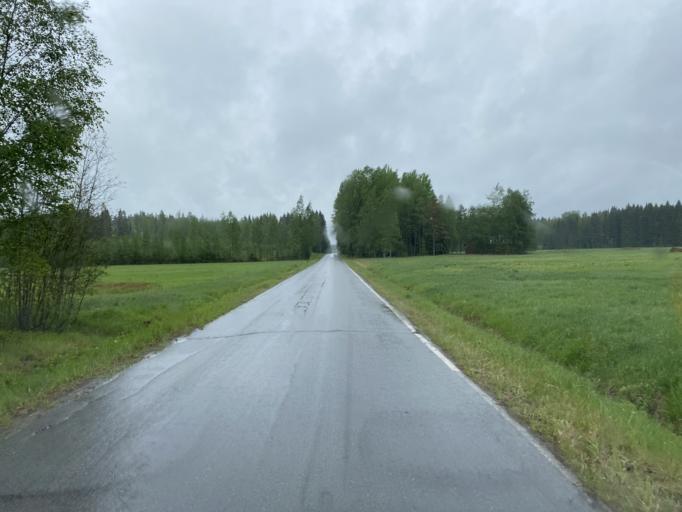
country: FI
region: Haeme
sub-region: Forssa
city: Humppila
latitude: 61.0631
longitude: 23.3241
